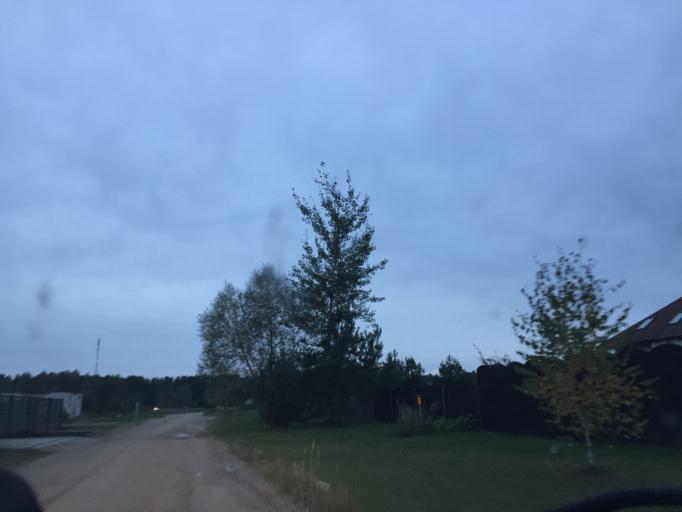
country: LV
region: Adazi
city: Adazi
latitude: 57.0865
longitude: 24.3754
